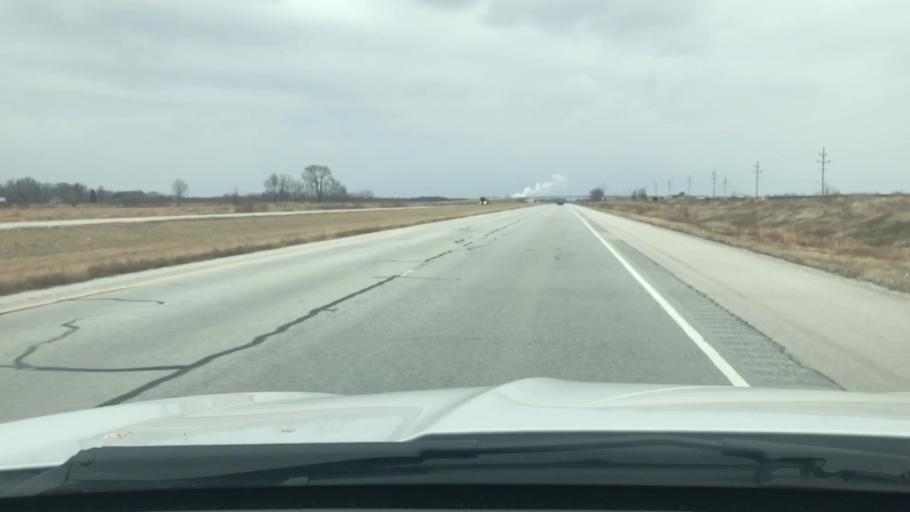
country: US
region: Indiana
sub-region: Cass County
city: Georgetown
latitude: 40.6854
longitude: -86.4915
